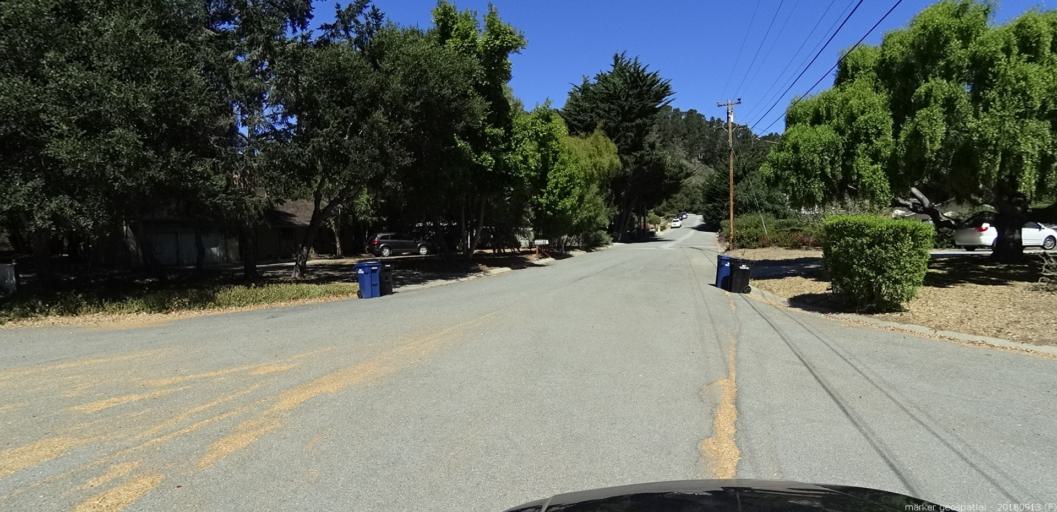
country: US
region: California
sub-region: Monterey County
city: Carmel-by-the-Sea
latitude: 36.5395
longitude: -121.8779
